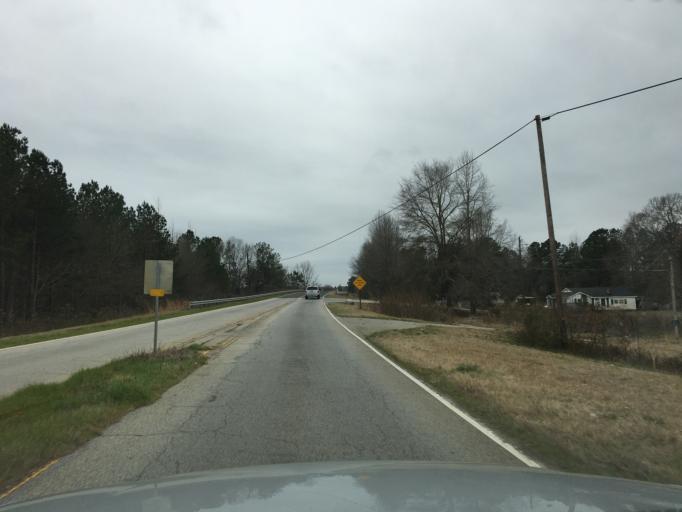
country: US
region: South Carolina
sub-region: Greenwood County
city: Greenwood
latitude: 34.1485
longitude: -82.1426
